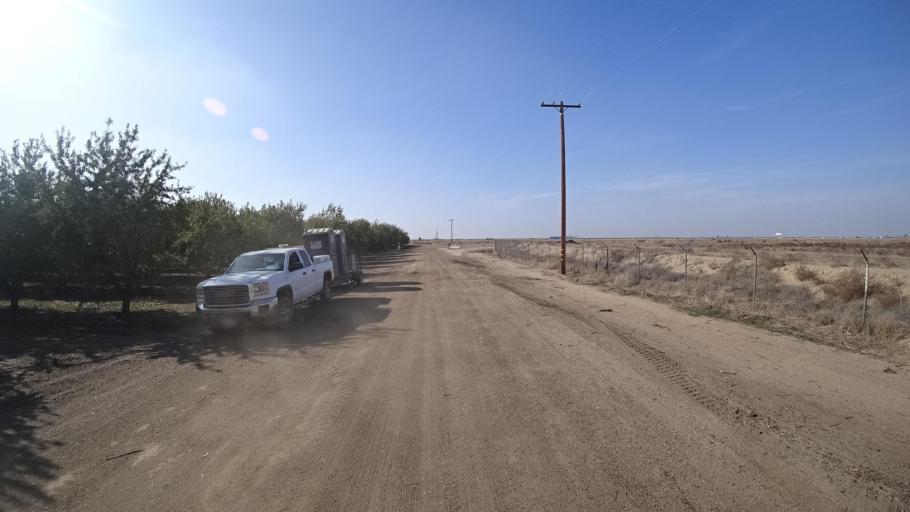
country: US
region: California
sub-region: Kern County
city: McFarland
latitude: 35.6308
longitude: -119.2121
